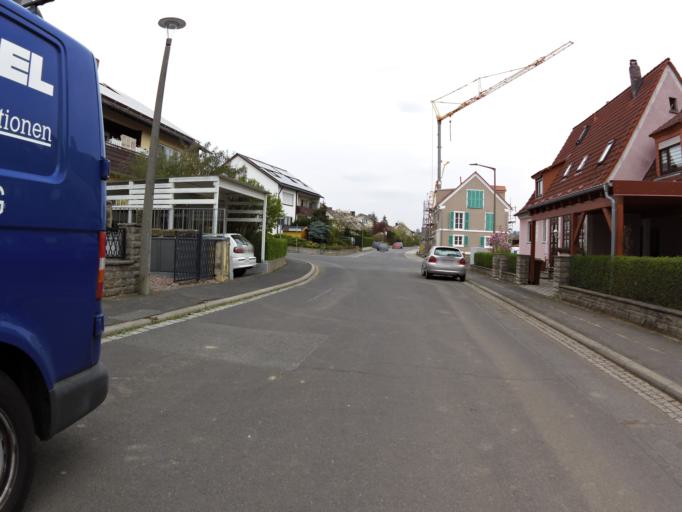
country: DE
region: Bavaria
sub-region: Regierungsbezirk Unterfranken
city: Rottendorf
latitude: 49.7945
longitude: 10.0212
